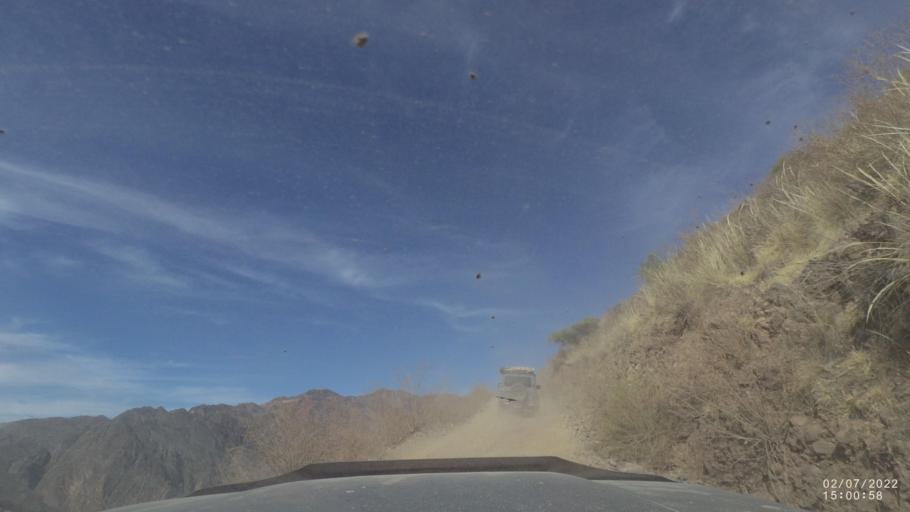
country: BO
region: Cochabamba
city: Irpa Irpa
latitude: -17.8527
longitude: -66.4420
